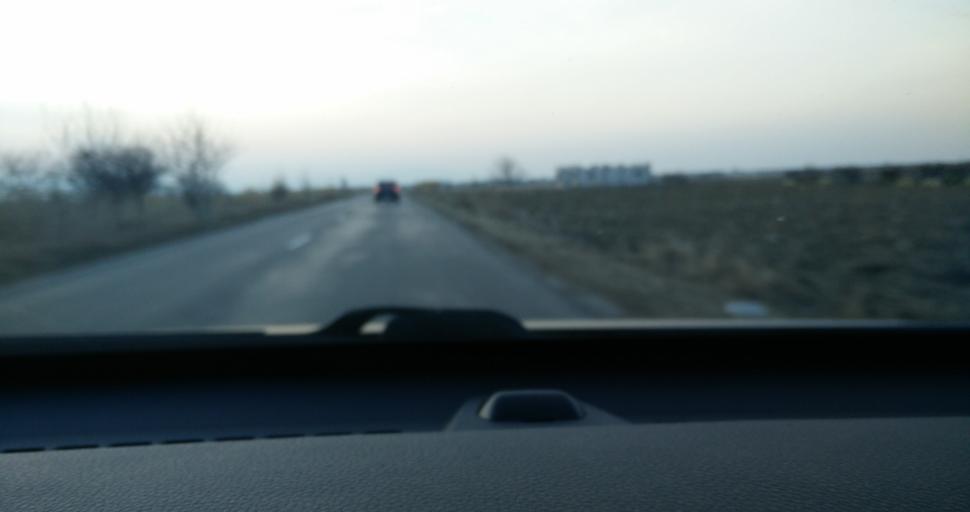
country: RO
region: Vrancea
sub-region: Comuna Milcovul
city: Milcovul
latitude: 45.6691
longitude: 27.2630
